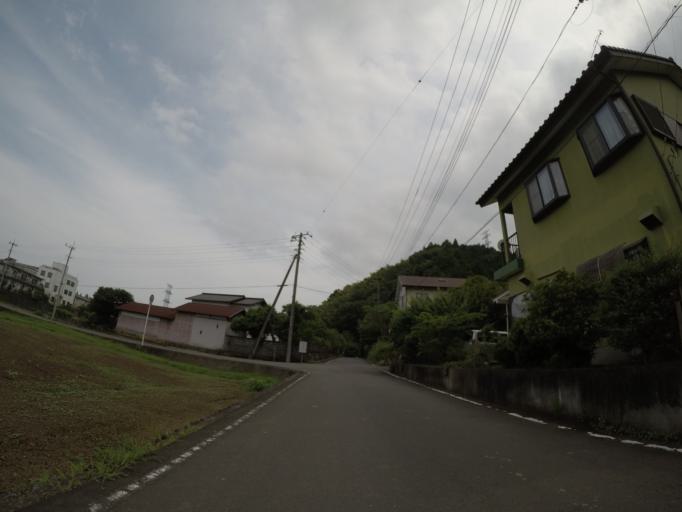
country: JP
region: Shizuoka
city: Fujinomiya
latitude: 35.2479
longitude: 138.5537
